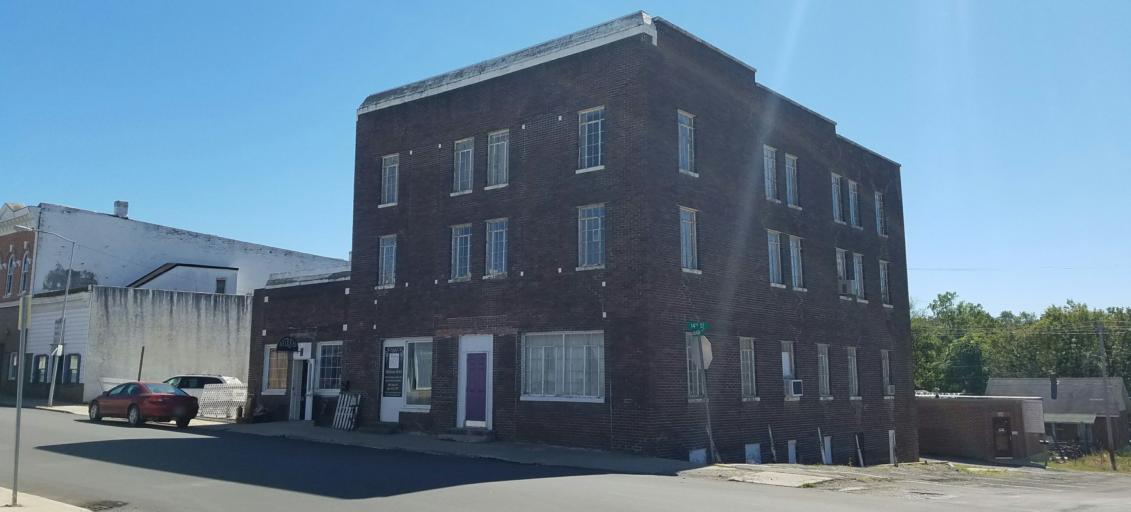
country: US
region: Missouri
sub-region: Harrison County
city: Bethany
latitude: 40.2689
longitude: -94.0366
